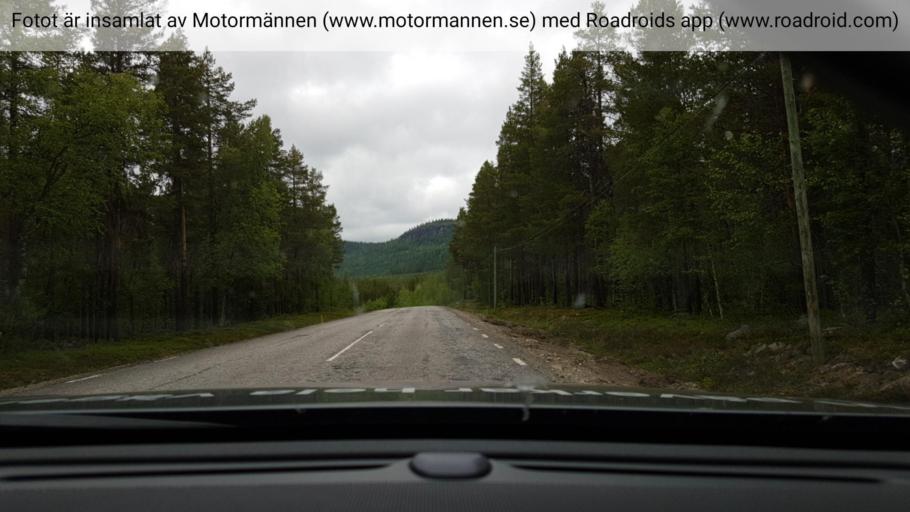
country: SE
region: Vaesterbotten
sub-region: Sorsele Kommun
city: Sorsele
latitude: 65.7564
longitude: 17.0844
